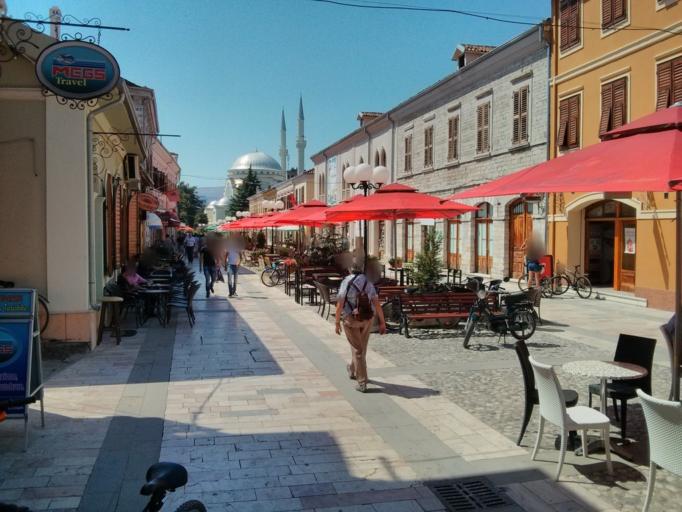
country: AL
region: Shkoder
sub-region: Rrethi i Shkodres
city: Shkoder
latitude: 42.0686
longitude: 19.5161
